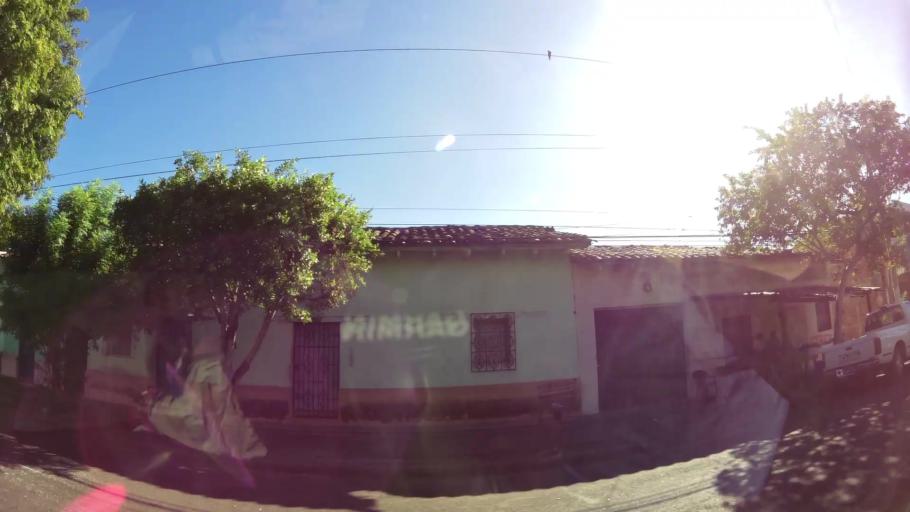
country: SV
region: San Miguel
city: San Miguel
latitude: 13.4699
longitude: -88.1787
